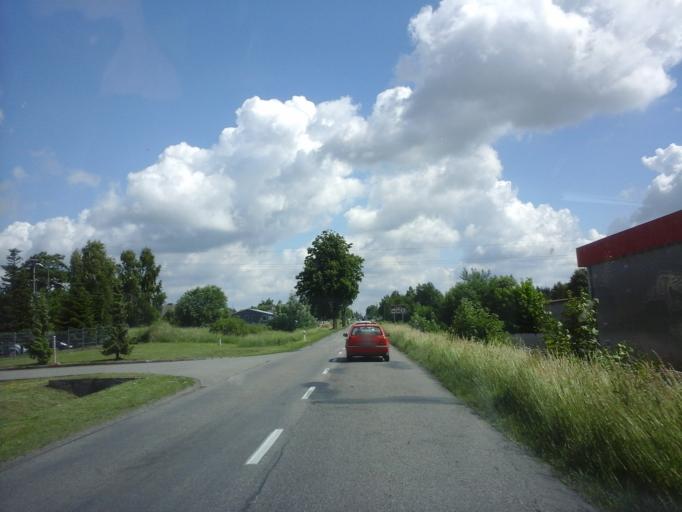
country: PL
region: West Pomeranian Voivodeship
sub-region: Powiat swidwinski
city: Swidwin
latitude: 53.7614
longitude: 15.7489
